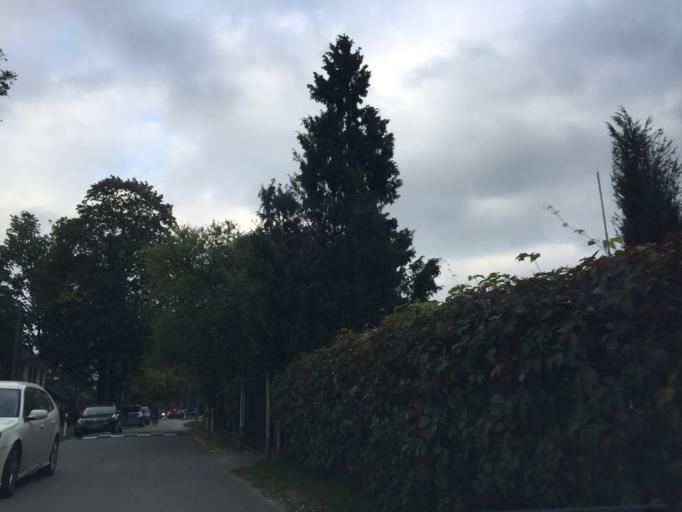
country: LV
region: Marupe
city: Marupe
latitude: 56.9507
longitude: 24.0230
